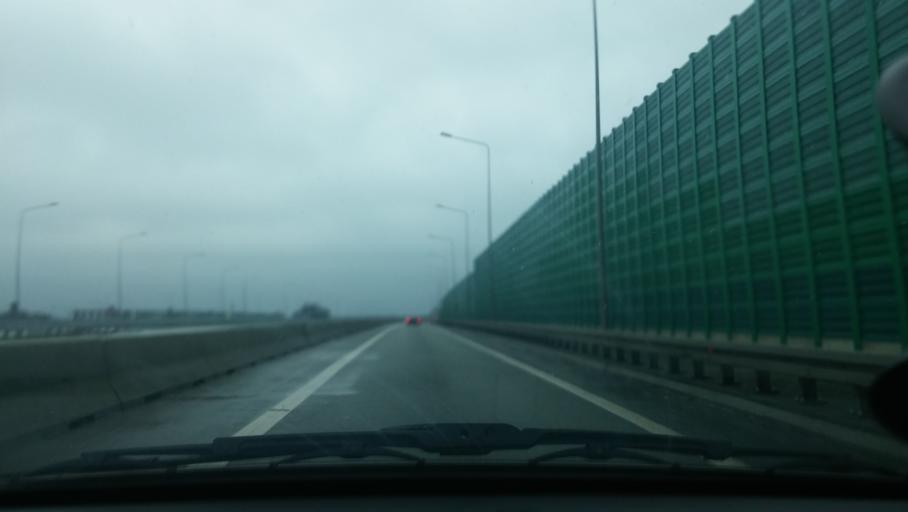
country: PL
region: Masovian Voivodeship
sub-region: Powiat minski
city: Kaluszyn
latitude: 52.1990
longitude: 21.7701
